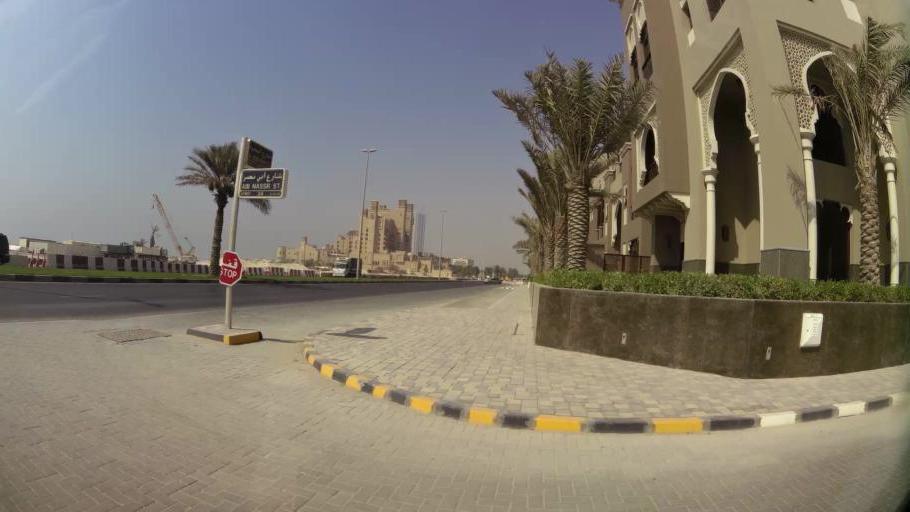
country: AE
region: Ajman
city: Ajman
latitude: 25.3929
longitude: 55.4205
